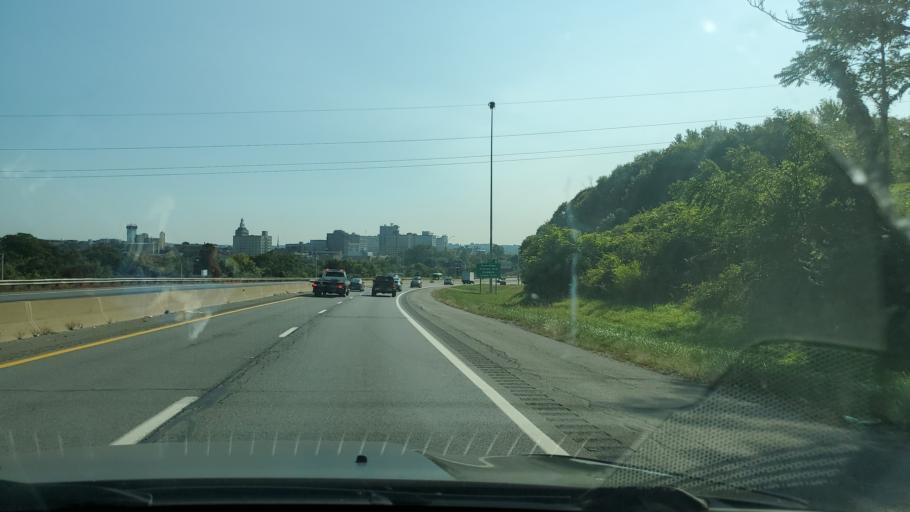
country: US
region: Ohio
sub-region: Mahoning County
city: Youngstown
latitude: 41.1000
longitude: -80.6647
